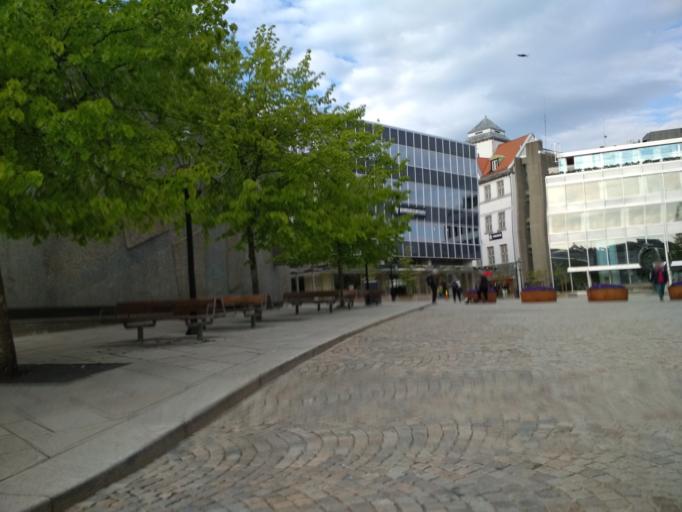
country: NO
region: Rogaland
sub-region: Stavanger
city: Stavanger
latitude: 58.9699
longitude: 5.7326
